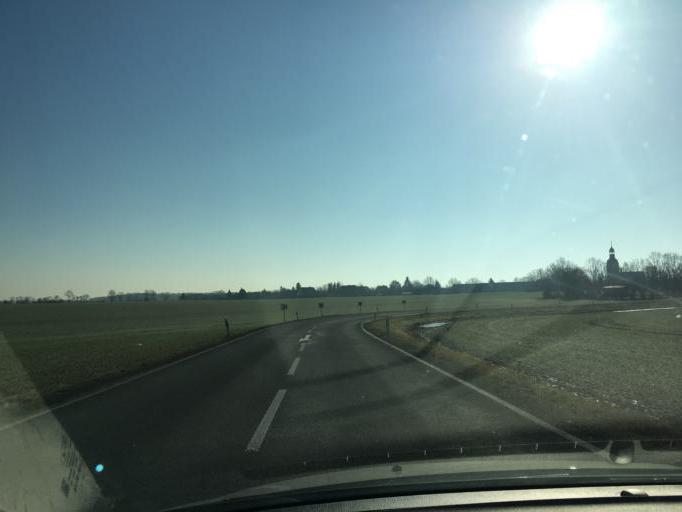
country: DE
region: Saxony
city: Otterwisch
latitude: 51.1776
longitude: 12.6200
